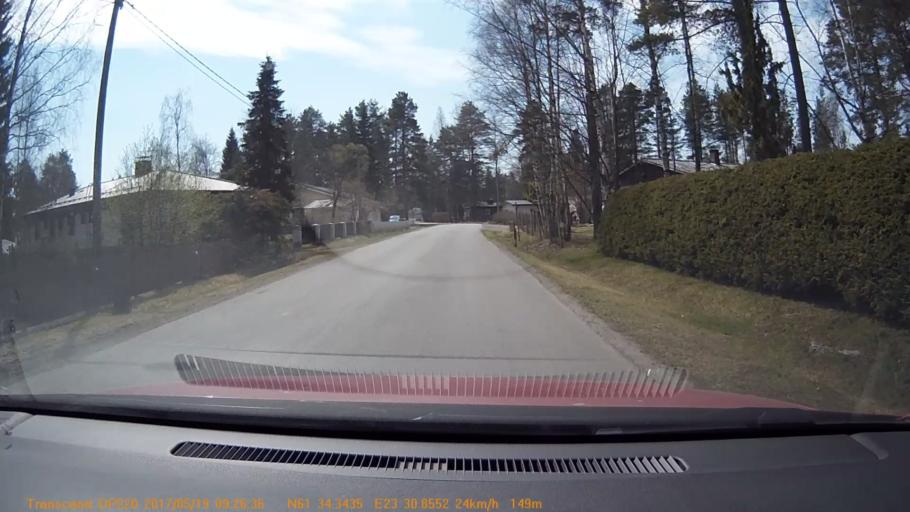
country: FI
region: Pirkanmaa
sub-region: Tampere
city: Yloejaervi
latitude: 61.5724
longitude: 23.5143
